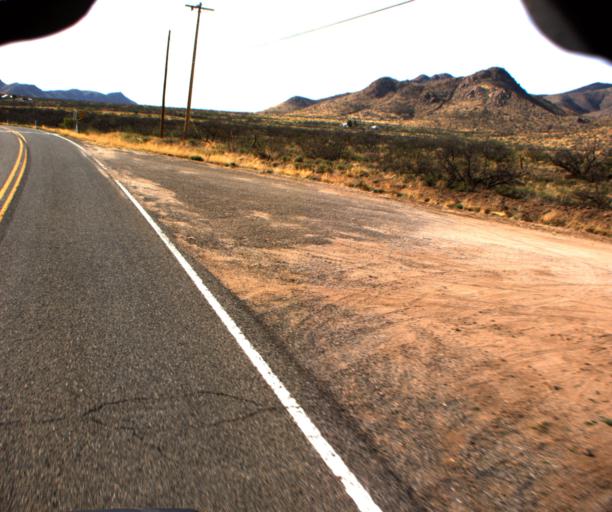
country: US
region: Arizona
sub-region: Cochise County
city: Willcox
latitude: 32.1741
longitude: -109.6040
